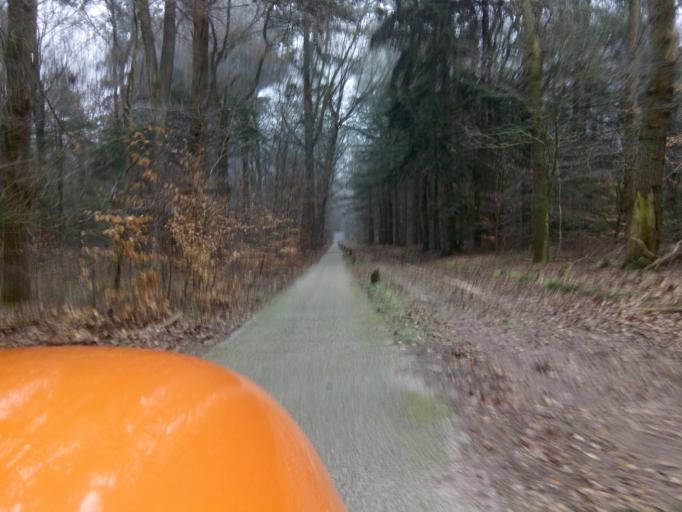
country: NL
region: Gelderland
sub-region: Gemeente Ermelo
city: Ermelo
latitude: 52.2707
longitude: 5.6556
